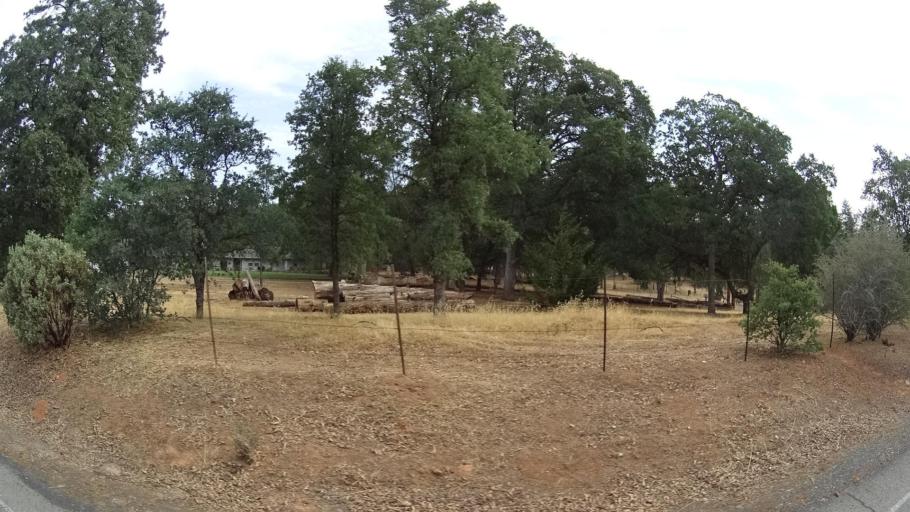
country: US
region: California
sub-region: Mariposa County
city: Midpines
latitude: 37.5327
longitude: -119.9497
